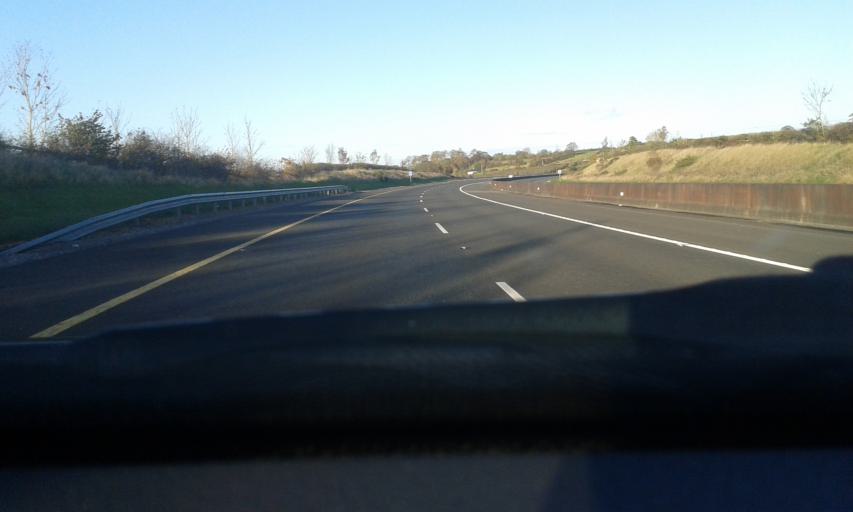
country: IE
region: Leinster
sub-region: Laois
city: Rathdowney
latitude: 52.7543
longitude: -7.5728
